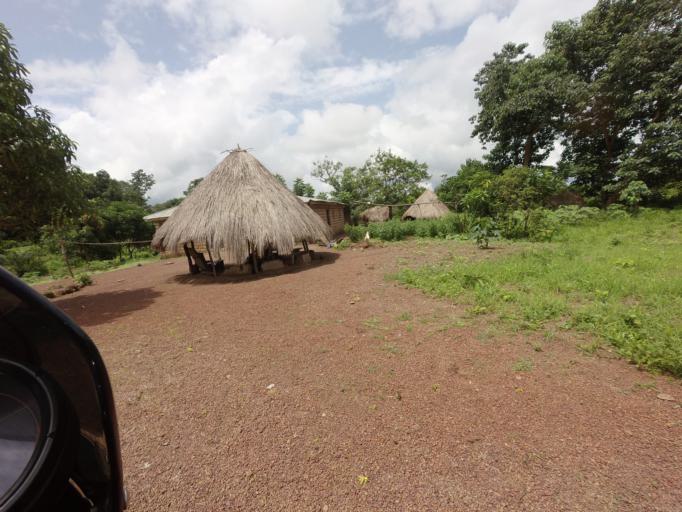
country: SL
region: Northern Province
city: Kukuna
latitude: 9.4582
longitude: -12.6395
